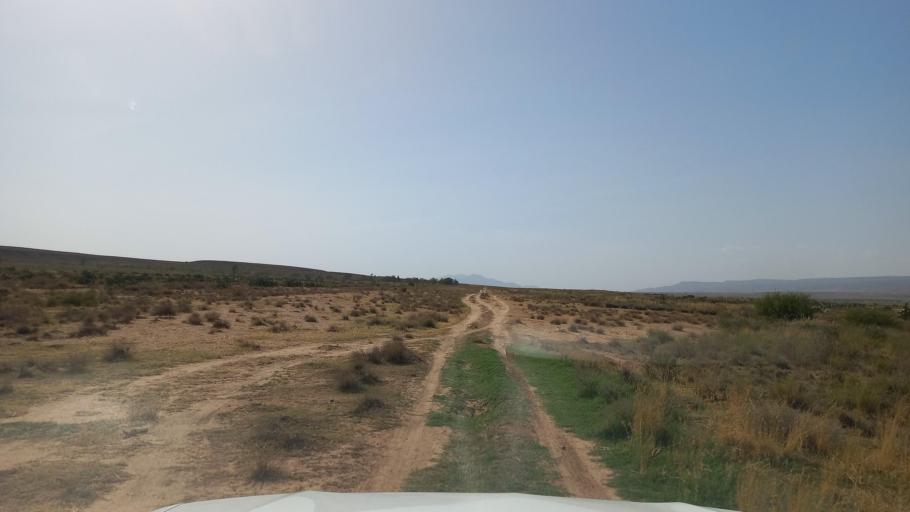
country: TN
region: Al Qasrayn
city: Kasserine
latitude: 35.2142
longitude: 9.0036
